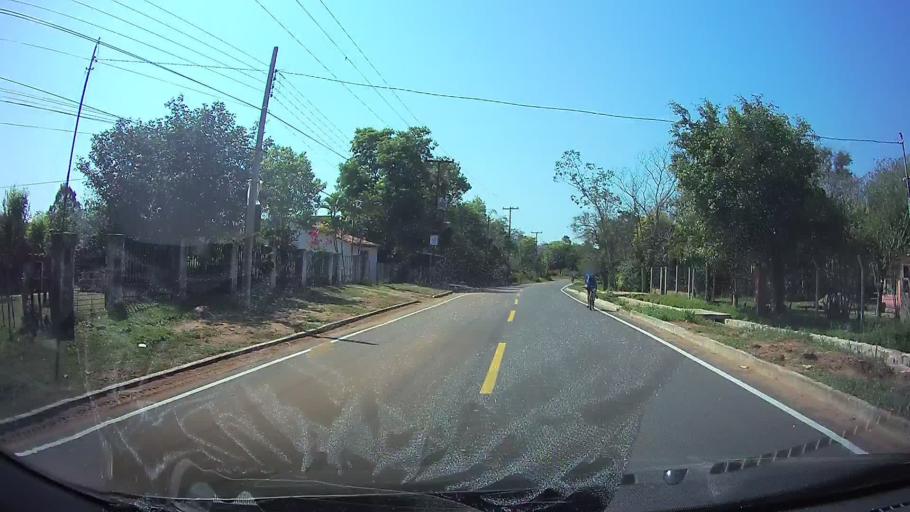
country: PY
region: Central
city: Limpio
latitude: -25.2356
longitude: -57.4905
